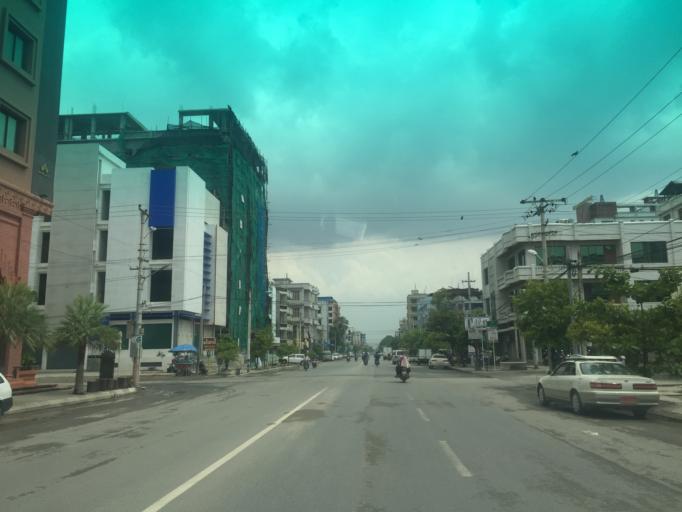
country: MM
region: Mandalay
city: Mandalay
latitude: 21.9798
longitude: 96.0957
